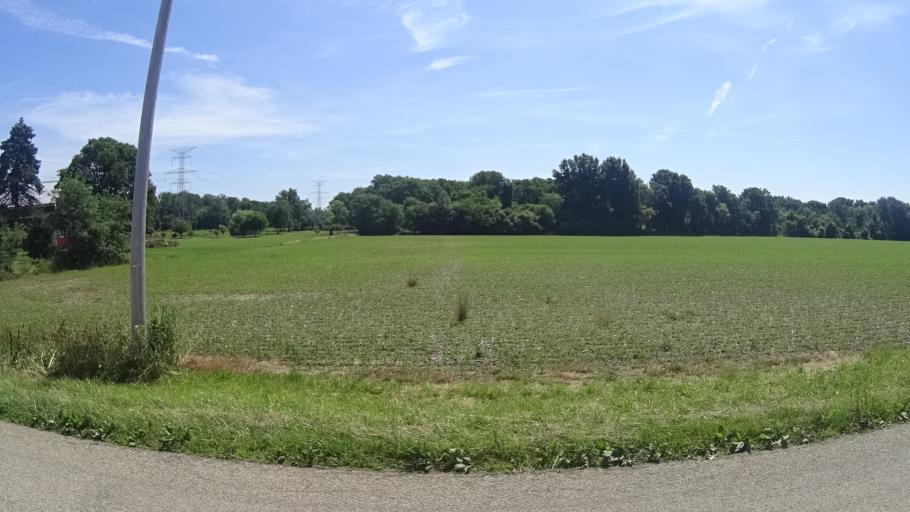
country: US
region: Ohio
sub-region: Huron County
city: Wakeman
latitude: 41.3353
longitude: -82.4590
